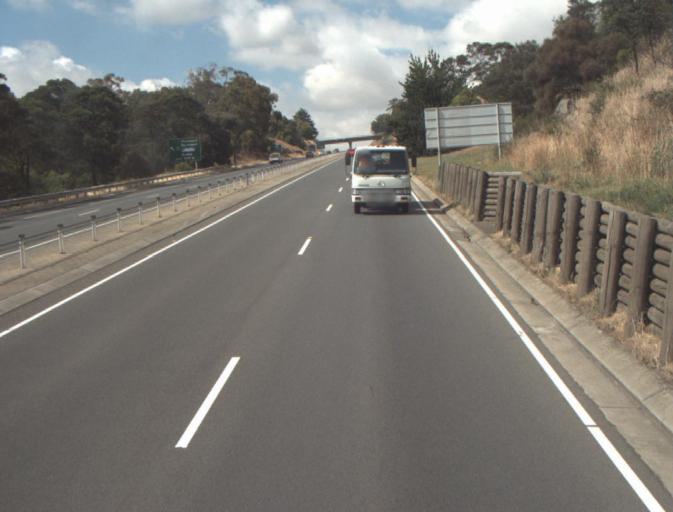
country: AU
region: Tasmania
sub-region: Launceston
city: Summerhill
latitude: -41.4621
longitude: 147.1427
